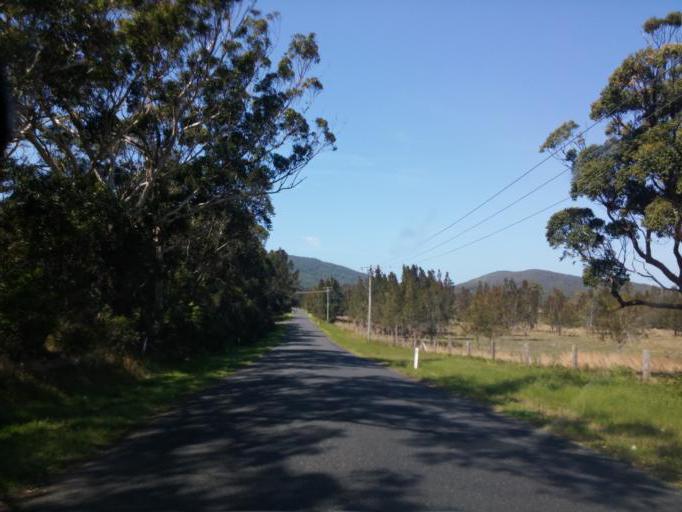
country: AU
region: New South Wales
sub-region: Great Lakes
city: Forster
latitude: -32.2134
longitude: 152.5354
